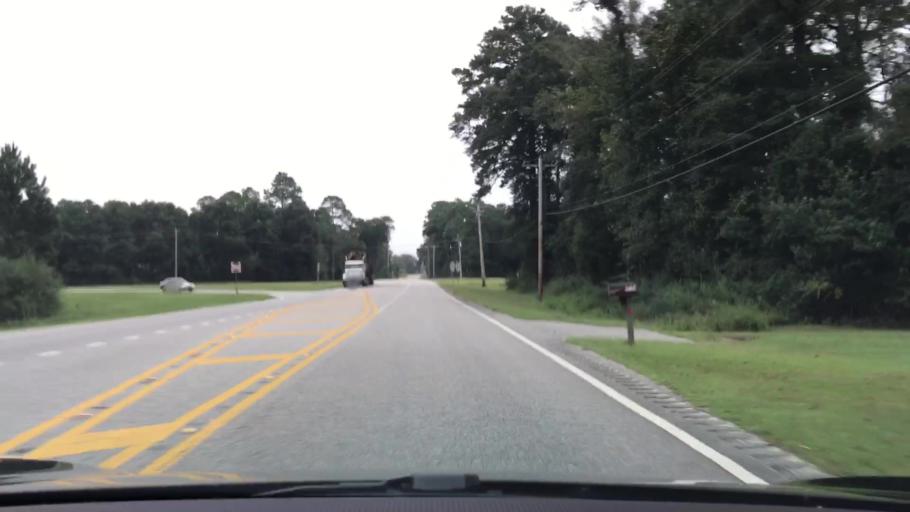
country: US
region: Alabama
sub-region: Coffee County
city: Elba
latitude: 31.4041
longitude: -86.0817
